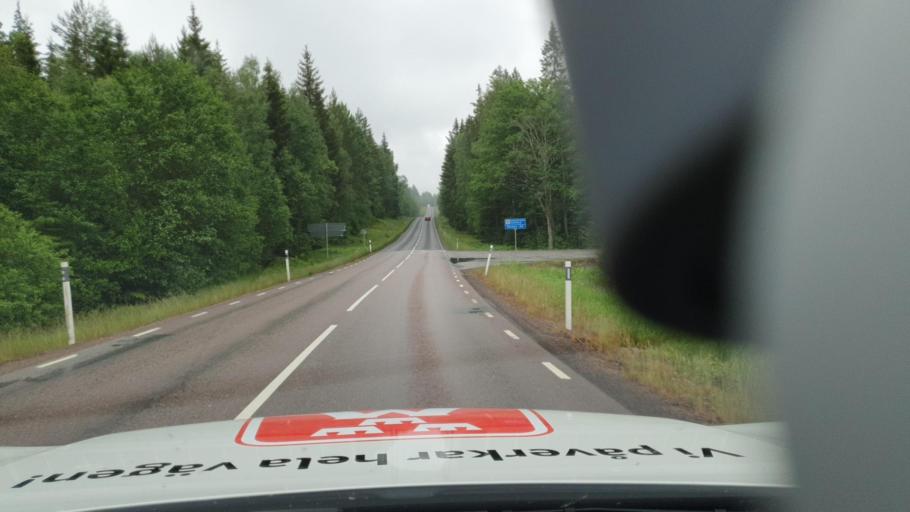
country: SE
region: Vaermland
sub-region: Kristinehamns Kommun
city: Bjorneborg
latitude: 59.2350
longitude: 14.2930
